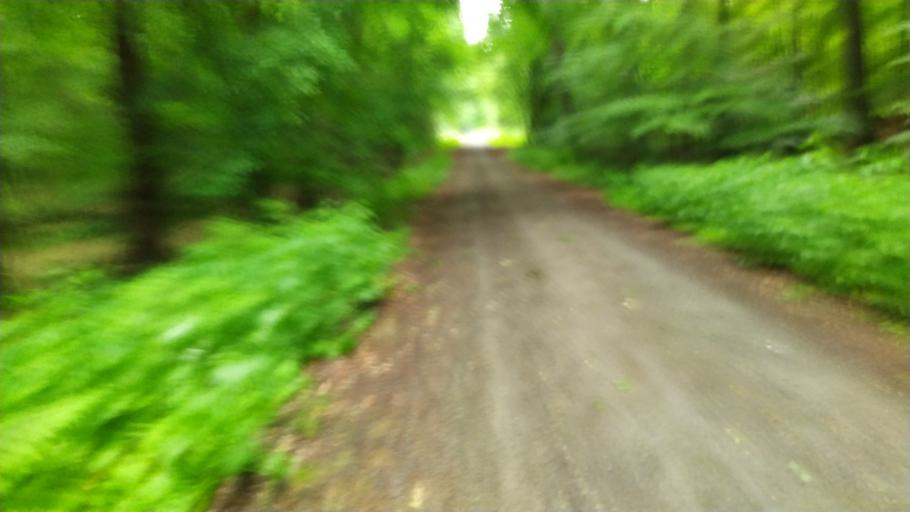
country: DE
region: Lower Saxony
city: Deinstedt
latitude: 53.4394
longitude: 9.2115
